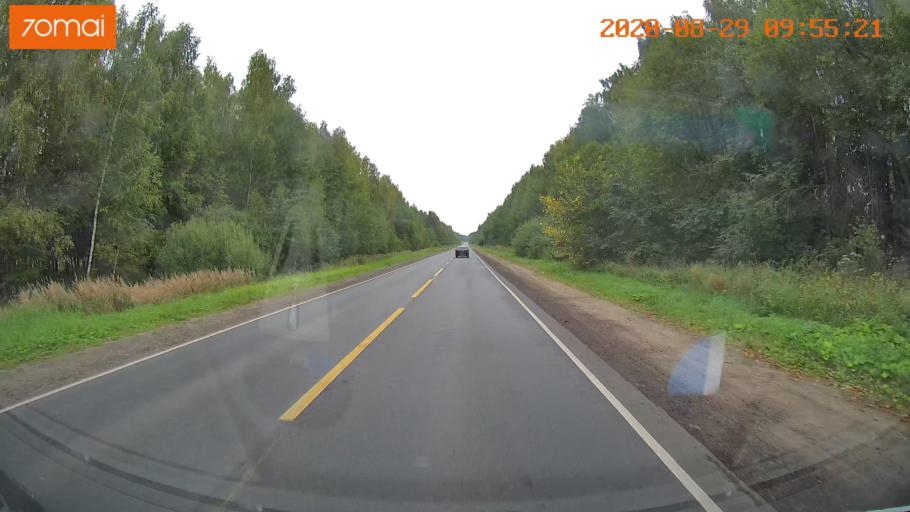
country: RU
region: Ivanovo
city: Zarechnyy
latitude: 57.4224
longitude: 42.2612
